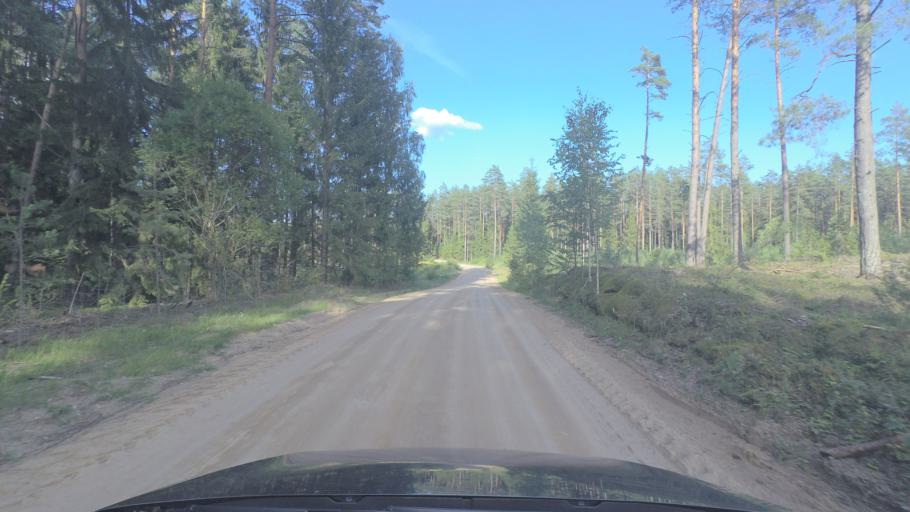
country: LT
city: Svencioneliai
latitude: 55.1653
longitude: 25.8315
